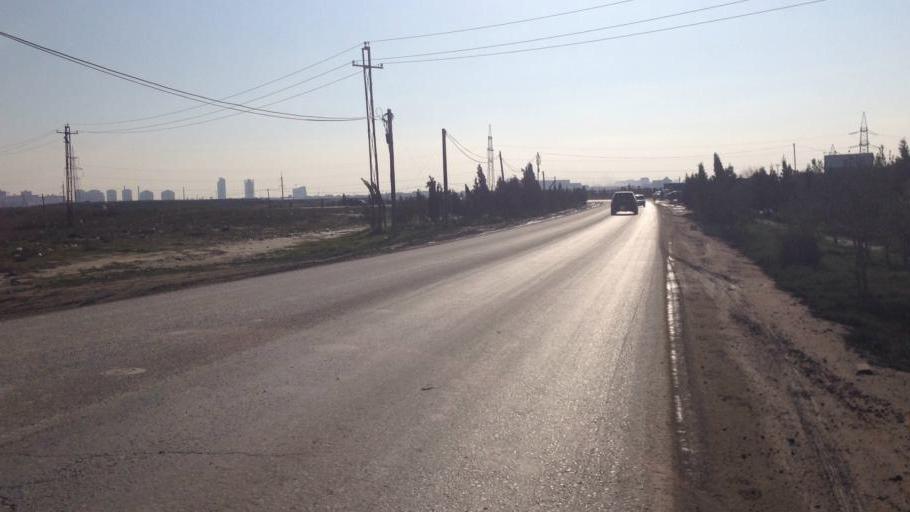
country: AZ
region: Baki
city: Balakhani
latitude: 40.4553
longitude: 49.8939
